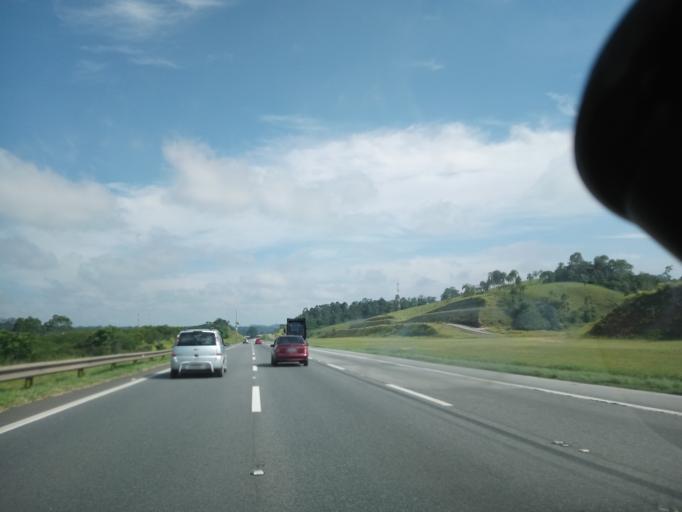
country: BR
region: Sao Paulo
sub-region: Itapecerica Da Serra
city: Itapecerica da Serra
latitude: -23.7044
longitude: -46.8123
